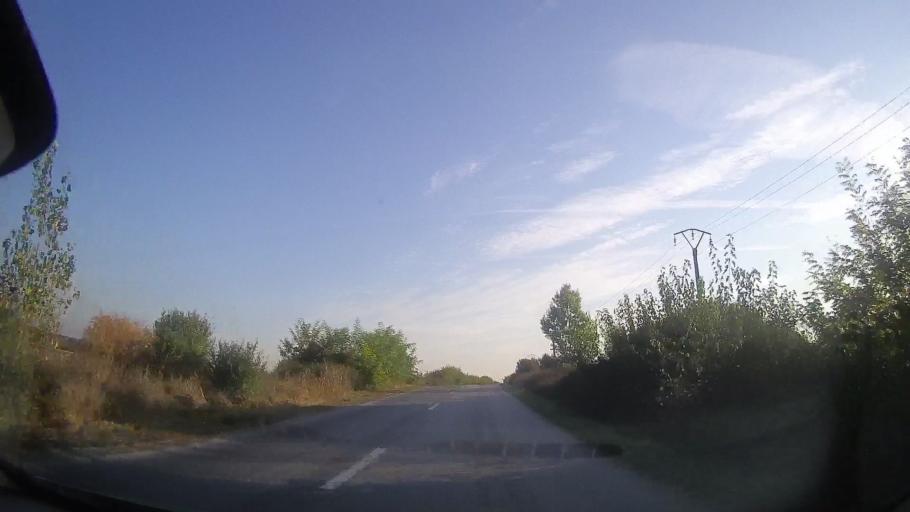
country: RO
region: Timis
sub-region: Comuna Pischia
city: Pischia
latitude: 45.8790
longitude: 21.3350
